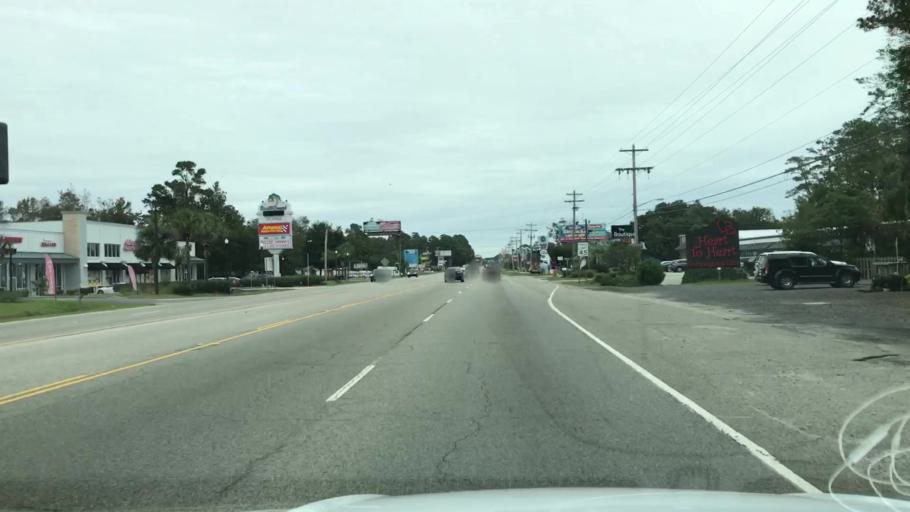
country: US
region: South Carolina
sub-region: Horry County
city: Garden City
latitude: 33.5801
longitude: -79.0203
